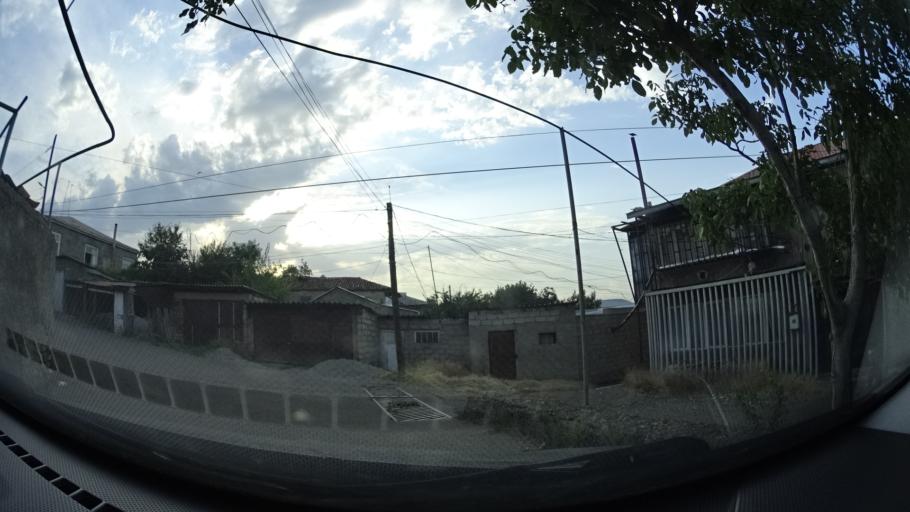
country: GE
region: Kakheti
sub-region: Telavi
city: Telavi
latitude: 41.9182
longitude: 45.4874
